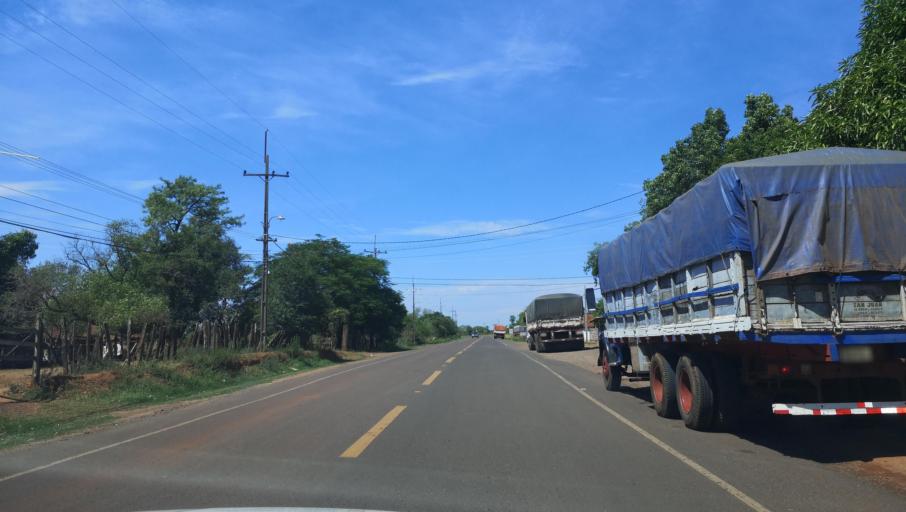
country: PY
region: Misiones
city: Santa Maria
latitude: -26.9018
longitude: -57.0283
